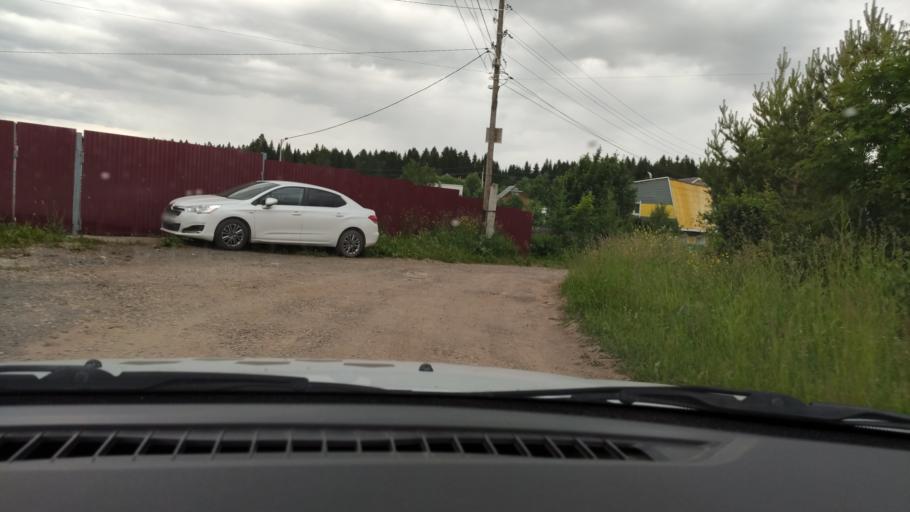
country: RU
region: Perm
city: Ferma
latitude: 57.9370
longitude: 56.3274
